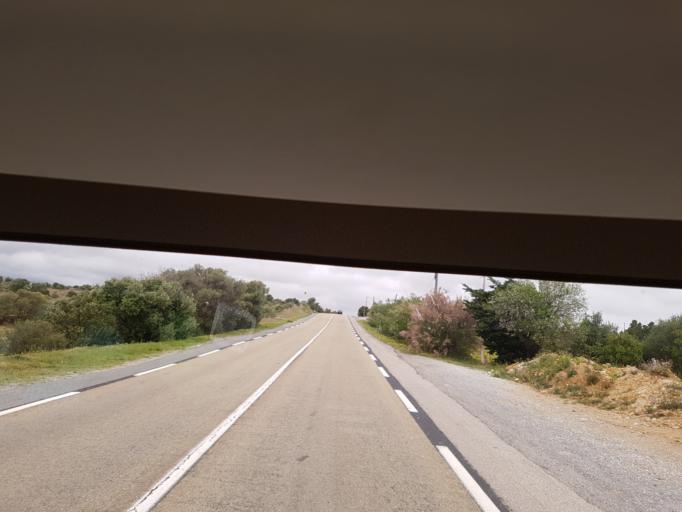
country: FR
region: Languedoc-Roussillon
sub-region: Departement de l'Aude
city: Leucate
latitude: 42.9040
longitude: 3.0009
